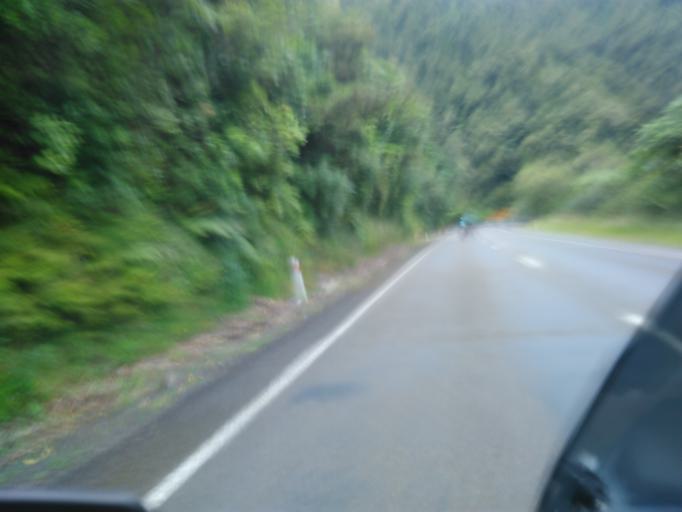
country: NZ
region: Bay of Plenty
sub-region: Opotiki District
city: Opotiki
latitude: -38.2701
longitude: 177.3195
